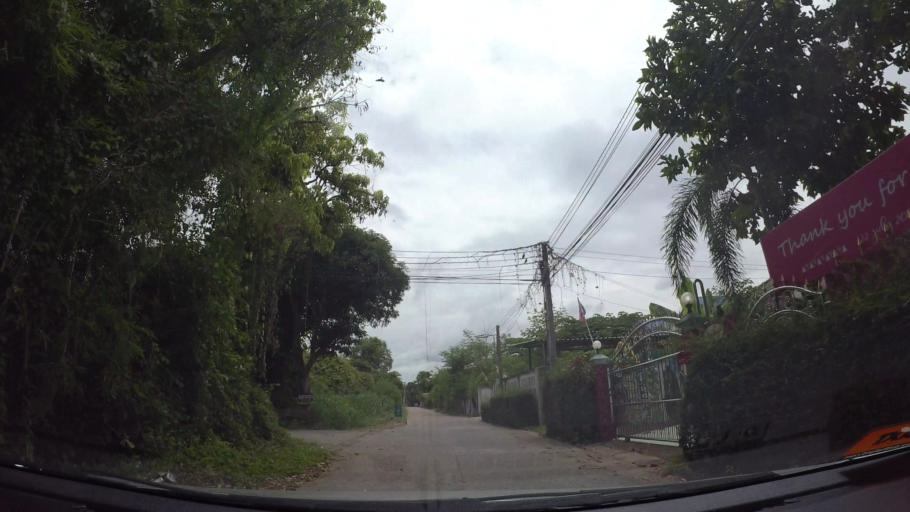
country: TH
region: Chon Buri
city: Sattahip
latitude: 12.6857
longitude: 100.8982
